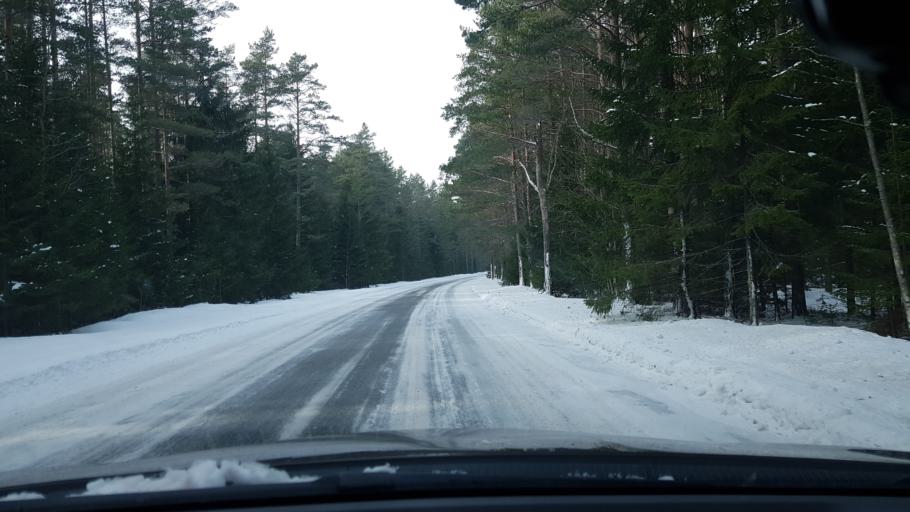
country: EE
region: Harju
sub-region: Kuusalu vald
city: Kuusalu
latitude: 59.5576
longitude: 25.5516
